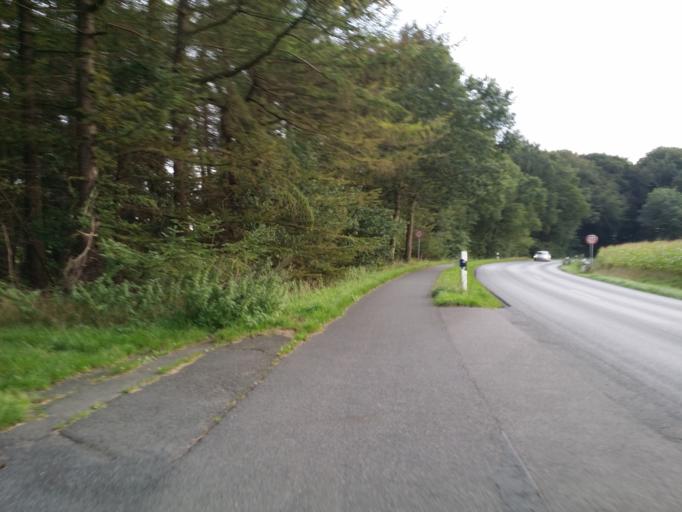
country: DE
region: Lower Saxony
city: Bremervorde
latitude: 53.4548
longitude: 9.1165
